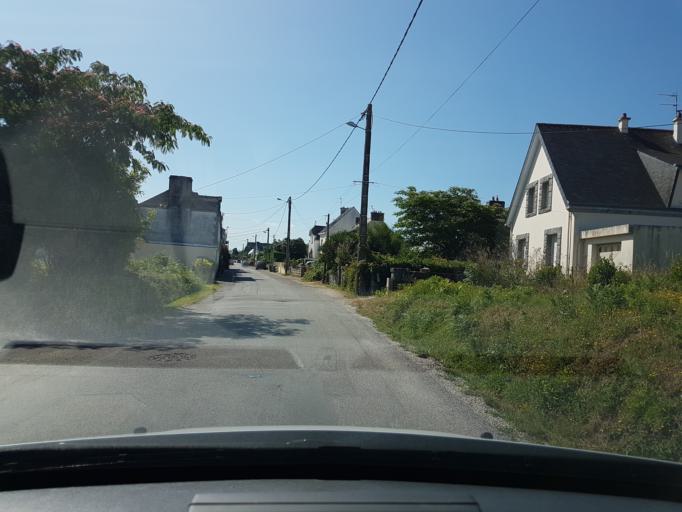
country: FR
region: Brittany
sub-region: Departement du Morbihan
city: Belz
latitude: 47.6809
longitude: -3.1848
